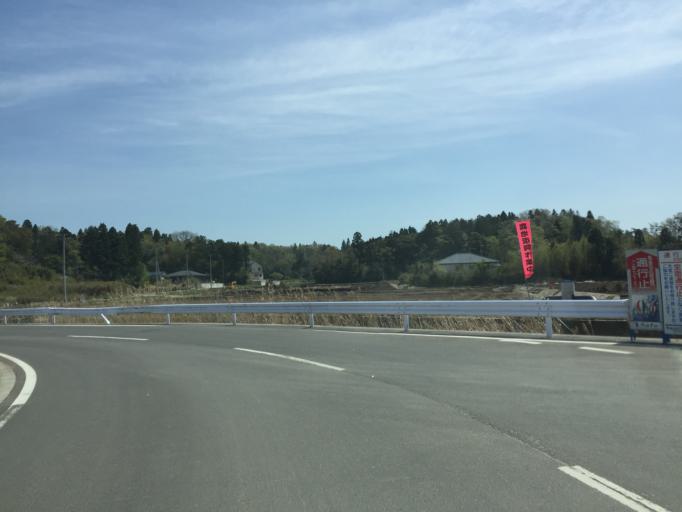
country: JP
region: Miyagi
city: Watari
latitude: 37.9000
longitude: 140.9245
